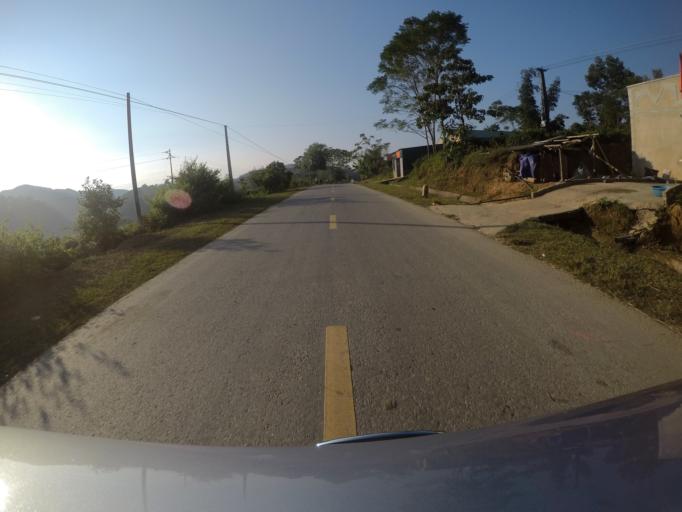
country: VN
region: Lai Chau
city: Than Uyen
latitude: 22.1290
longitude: 103.7923
